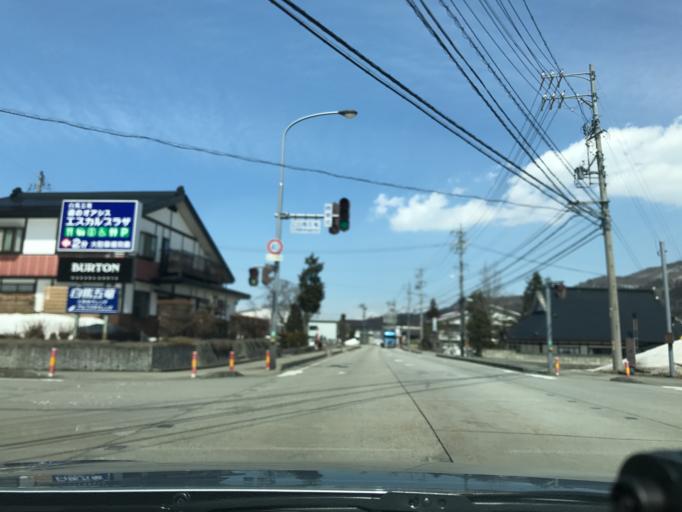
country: JP
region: Nagano
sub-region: Kitaazumi Gun
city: Hakuba
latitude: 36.6556
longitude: 137.8475
